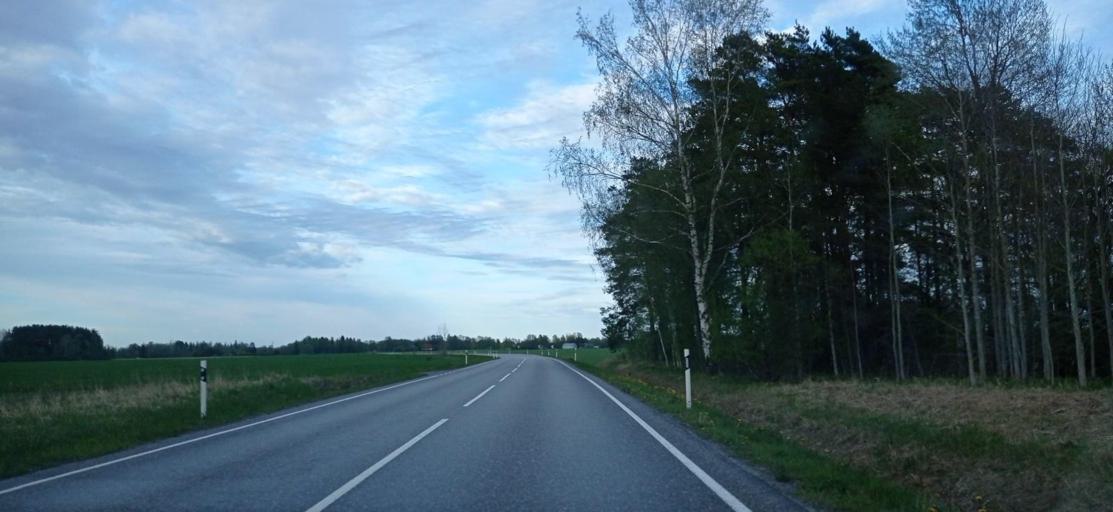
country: EE
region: Paernumaa
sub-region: Sindi linn
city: Sindi
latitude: 58.5273
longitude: 24.6742
